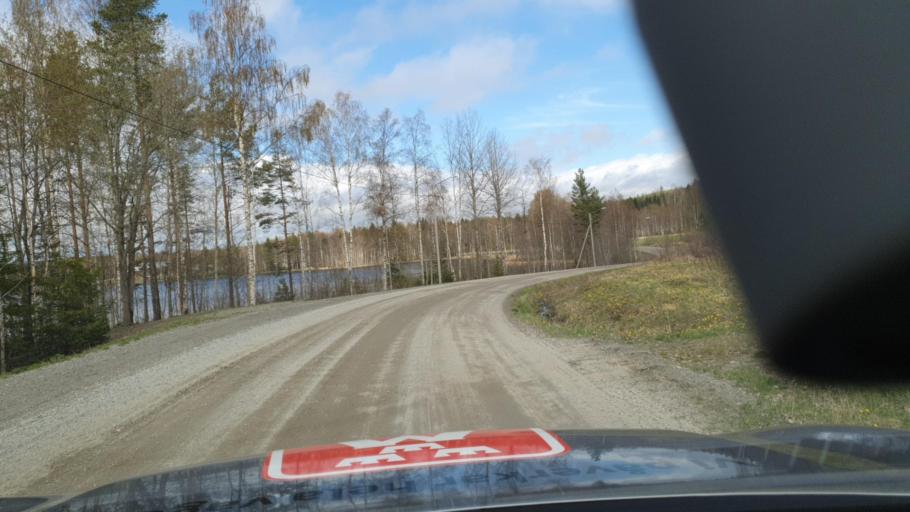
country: SE
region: Vaesterbotten
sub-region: Bjurholms Kommun
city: Bjurholm
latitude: 63.6908
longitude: 18.9570
